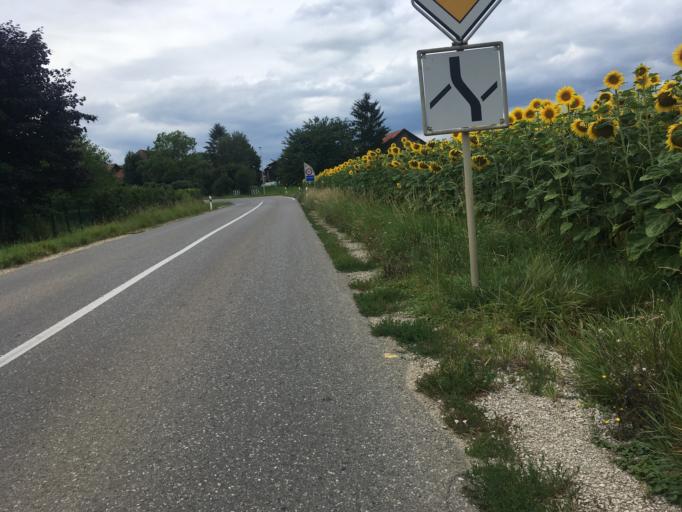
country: CH
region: Vaud
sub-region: Broye-Vully District
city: Payerne
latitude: 46.8720
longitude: 6.9485
